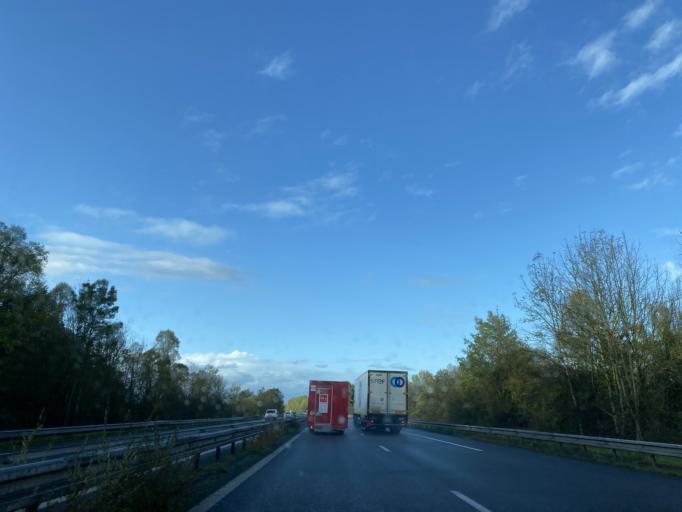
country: FR
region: Centre
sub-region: Departement du Cher
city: Foecy
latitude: 47.1725
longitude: 2.1796
